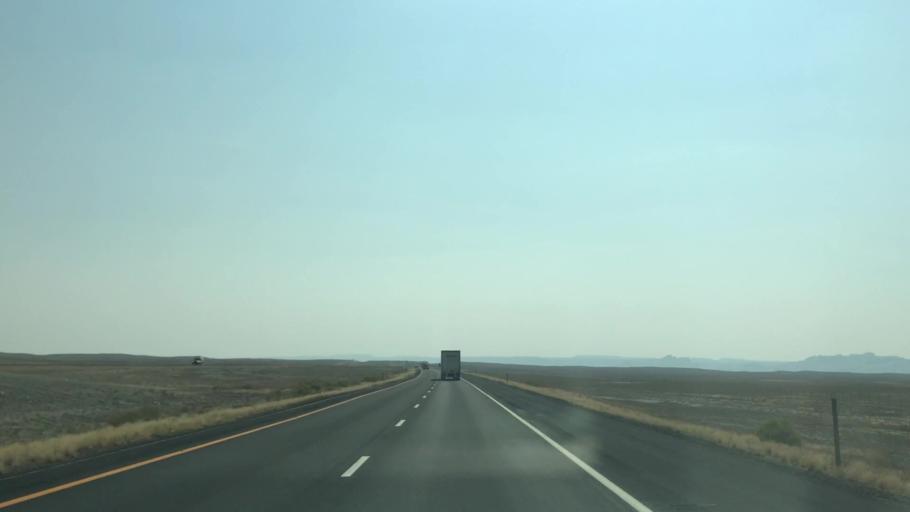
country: US
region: Utah
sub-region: Carbon County
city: East Carbon City
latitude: 38.9513
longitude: -110.3163
